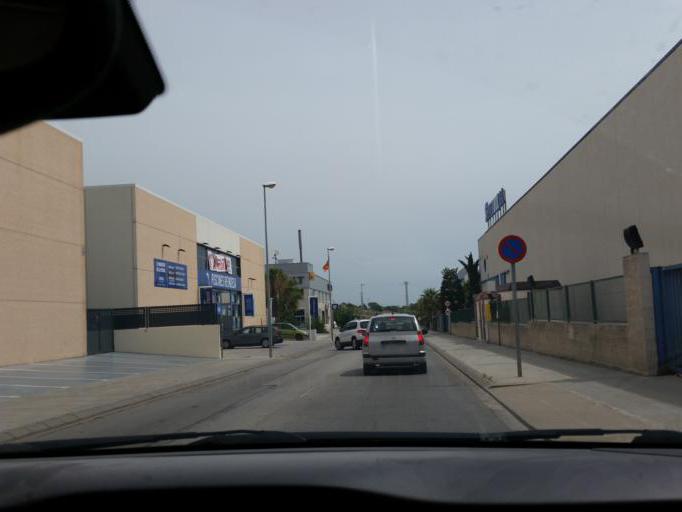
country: ES
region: Catalonia
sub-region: Provincia de Barcelona
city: Vilassar de Mar
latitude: 41.5145
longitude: 2.3871
